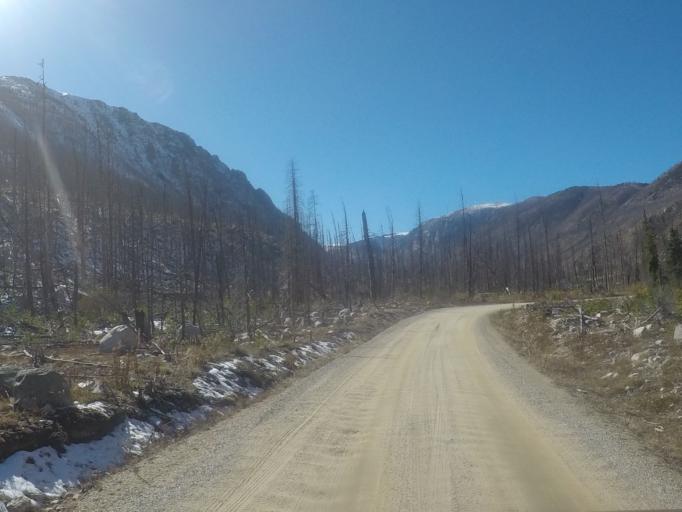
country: US
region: Montana
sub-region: Carbon County
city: Red Lodge
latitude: 45.1715
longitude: -109.4667
